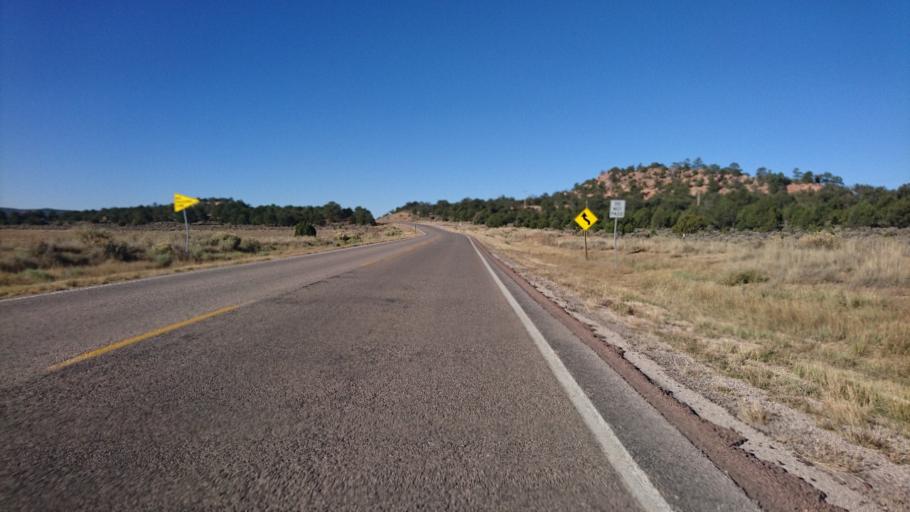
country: US
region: New Mexico
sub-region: McKinley County
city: Black Rock
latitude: 35.1257
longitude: -108.5331
